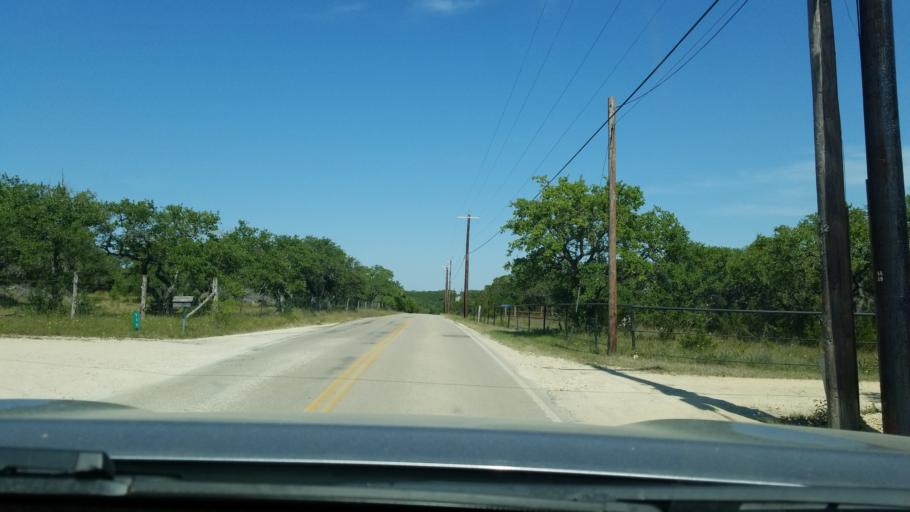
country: US
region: Texas
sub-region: Comal County
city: Bulverde
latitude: 29.7591
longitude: -98.5003
